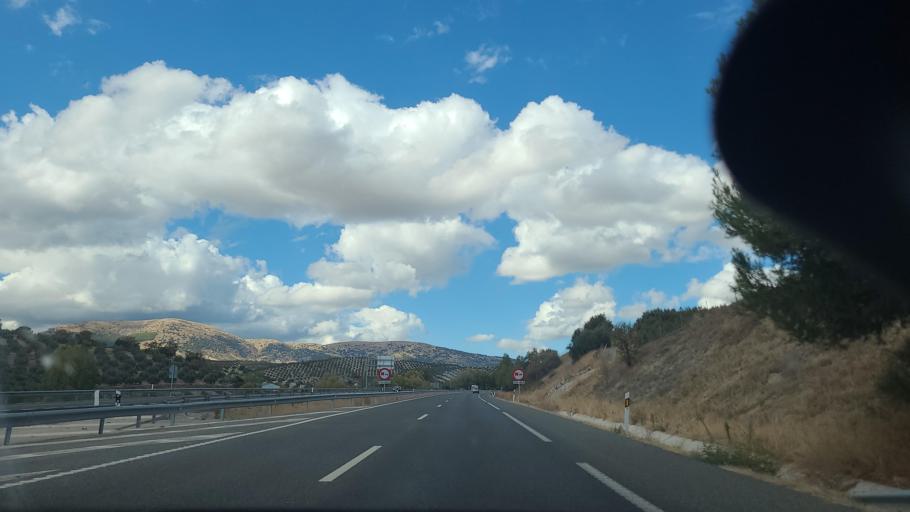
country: ES
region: Andalusia
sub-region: Provincia de Jaen
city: Noalejo
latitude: 37.5095
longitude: -3.6337
